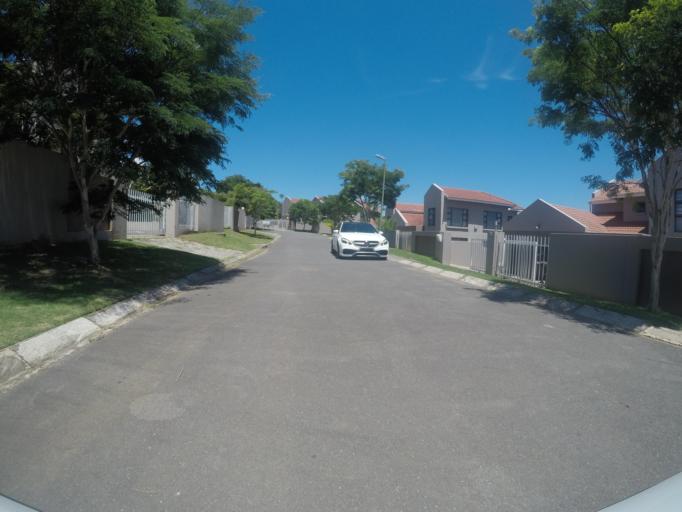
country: ZA
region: Eastern Cape
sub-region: Buffalo City Metropolitan Municipality
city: East London
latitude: -32.9274
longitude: 27.9985
